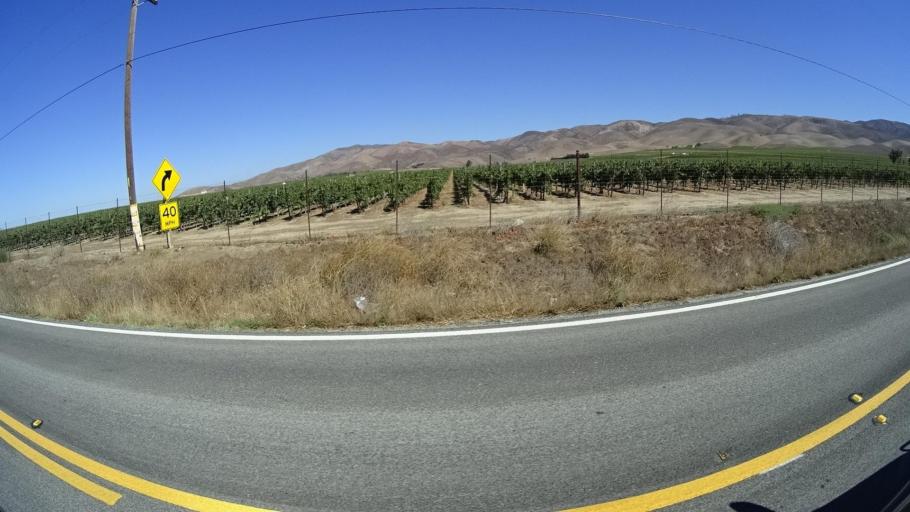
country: US
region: California
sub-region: Monterey County
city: Soledad
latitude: 36.4229
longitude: -121.2940
